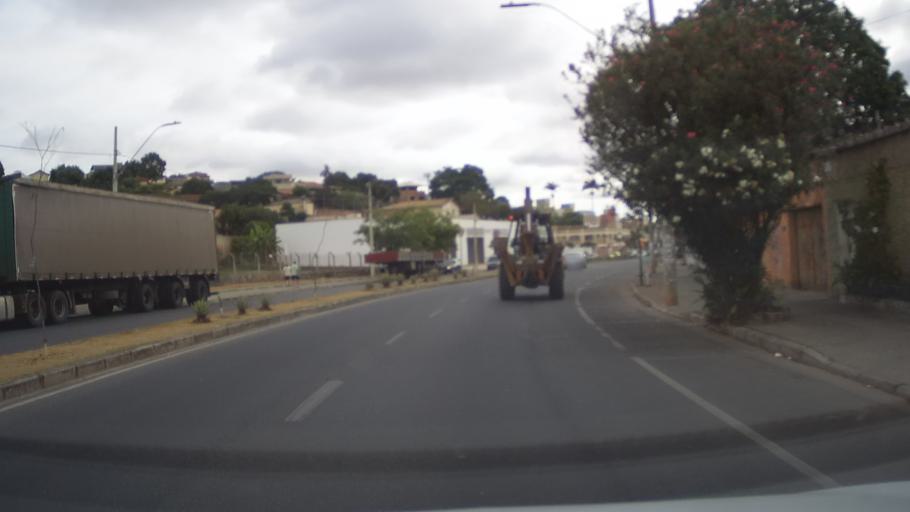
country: BR
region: Minas Gerais
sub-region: Belo Horizonte
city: Belo Horizonte
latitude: -19.8307
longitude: -43.9739
